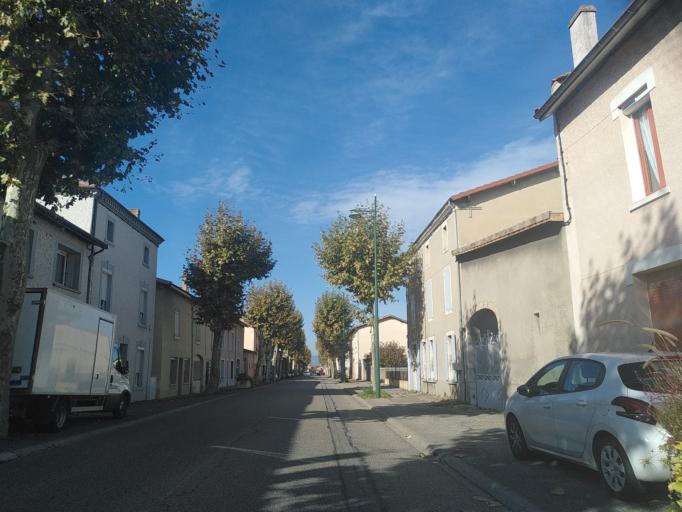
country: FR
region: Rhone-Alpes
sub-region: Departement de l'Isere
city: Chanas
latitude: 45.2866
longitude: 4.8167
